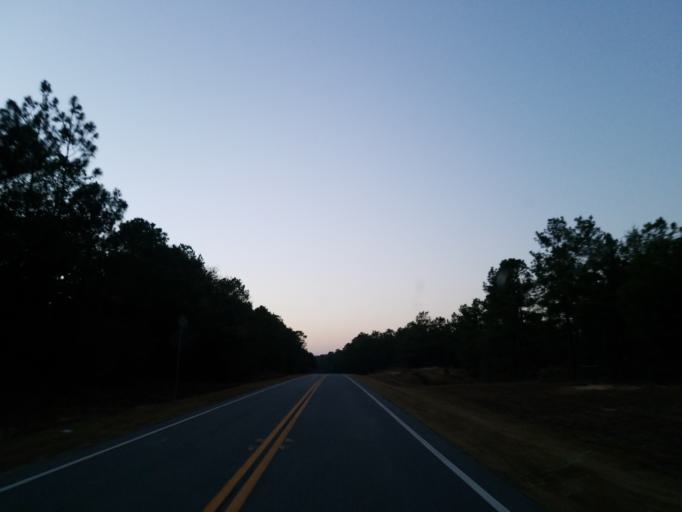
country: US
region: Georgia
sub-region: Wilcox County
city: Rochelle
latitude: 31.8187
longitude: -83.5376
